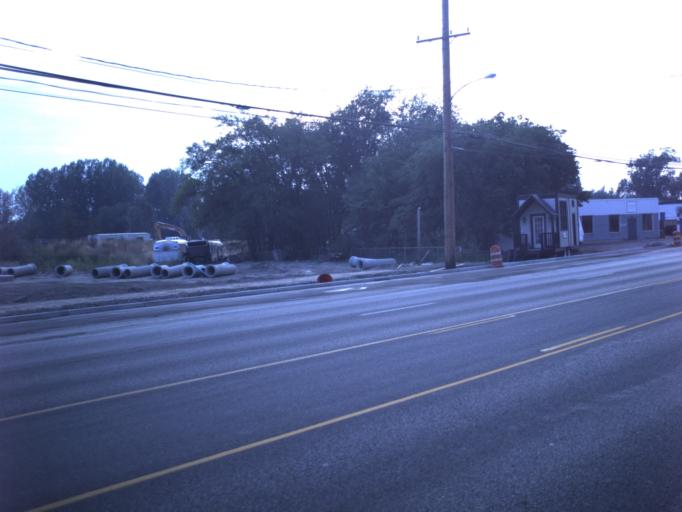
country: US
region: Utah
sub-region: Utah County
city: Provo
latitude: 40.2103
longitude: -111.6319
